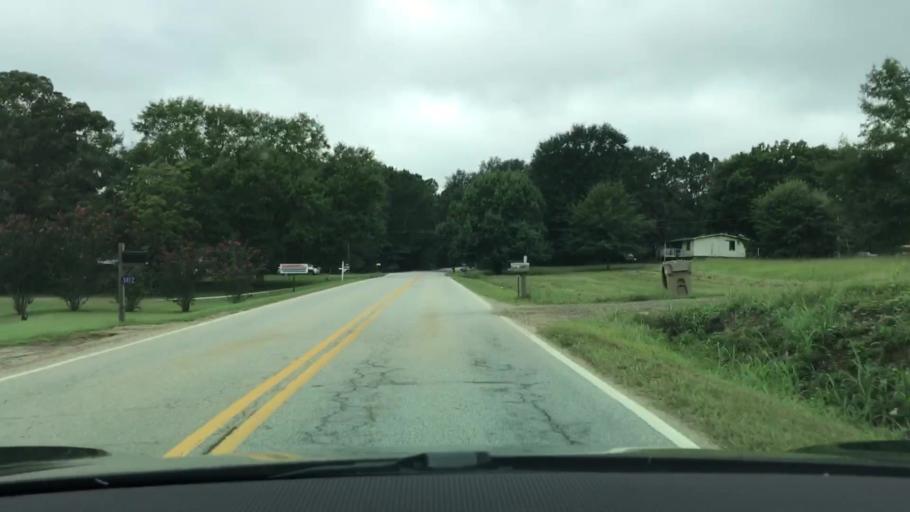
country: US
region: Georgia
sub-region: Barrow County
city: Auburn
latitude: 34.0565
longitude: -83.8275
